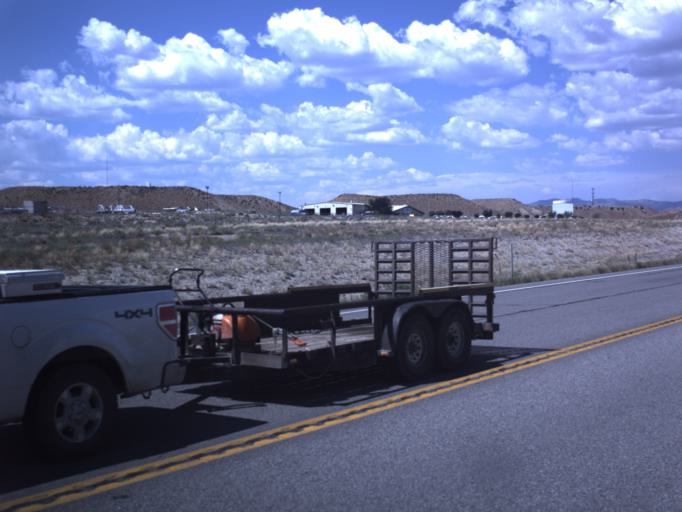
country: US
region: Utah
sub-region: Carbon County
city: Price
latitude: 39.5316
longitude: -110.8183
